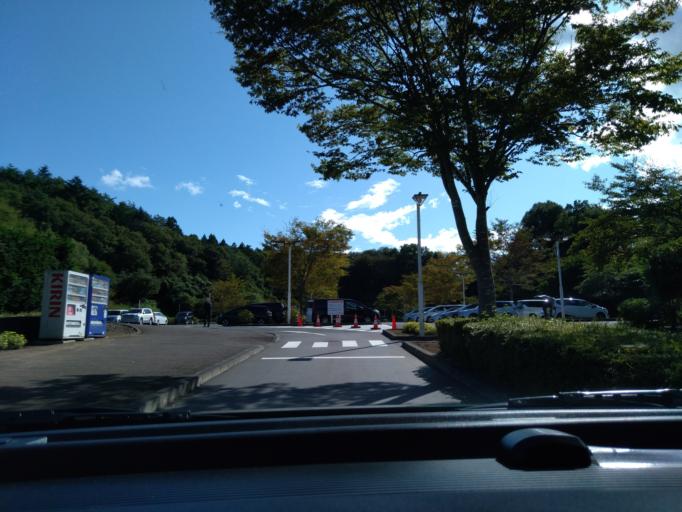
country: JP
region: Iwate
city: Ichinoseki
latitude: 38.7601
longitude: 141.1710
